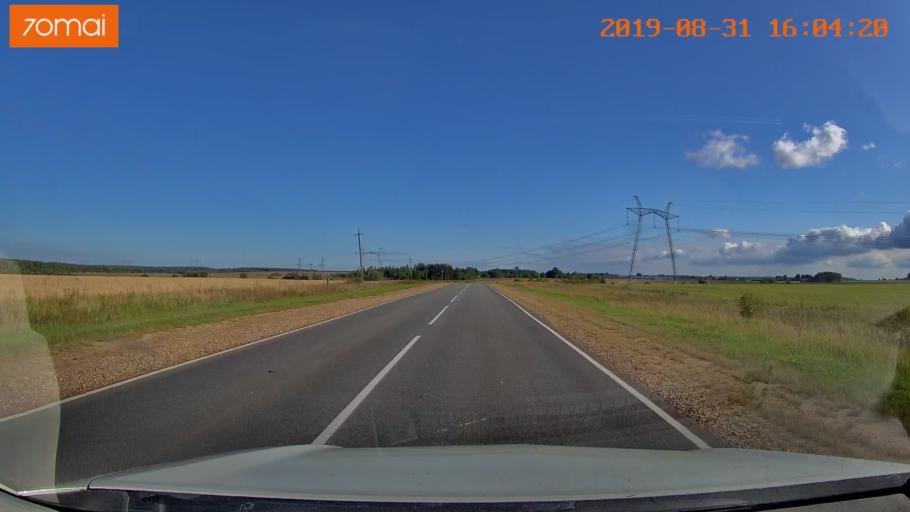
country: RU
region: Kaluga
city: Yukhnov
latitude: 54.6557
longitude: 35.3273
